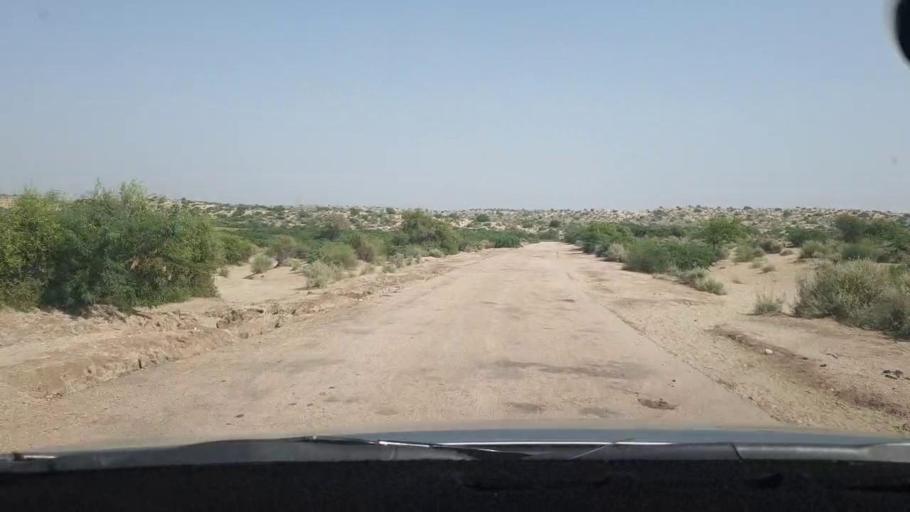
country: PK
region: Sindh
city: Pithoro
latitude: 25.7806
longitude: 69.4822
